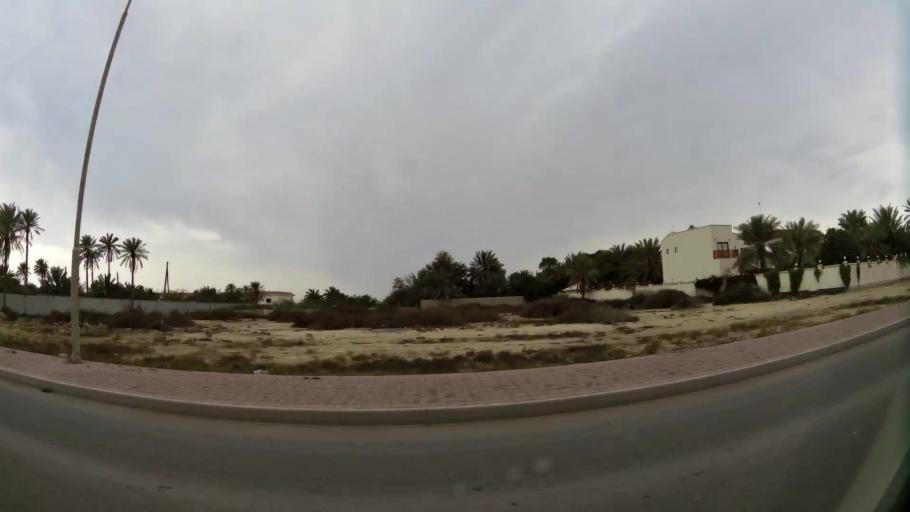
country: BH
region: Central Governorate
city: Madinat Hamad
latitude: 26.1616
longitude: 50.4510
